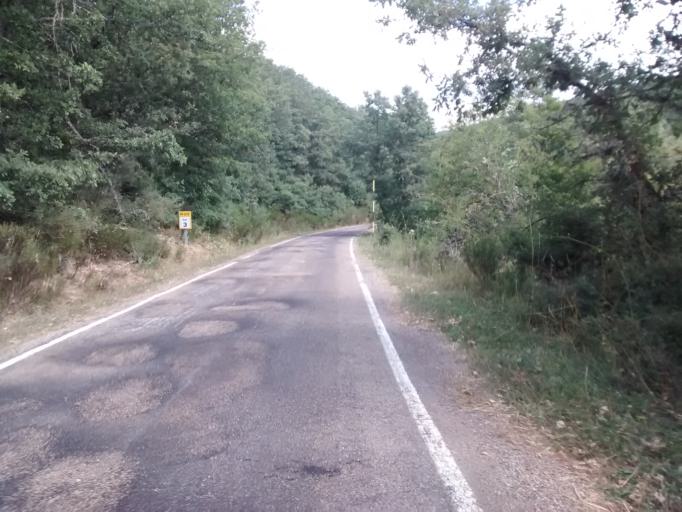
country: ES
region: Castille and Leon
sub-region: Provincia de Palencia
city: San Cebrian de Muda
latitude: 42.9287
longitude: -4.4506
